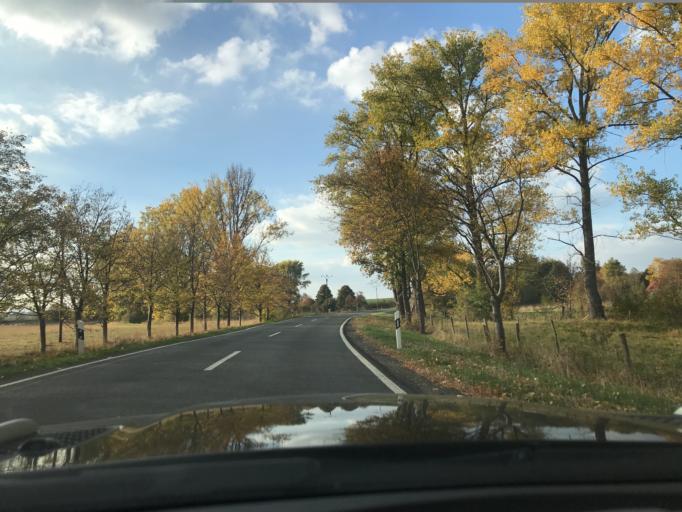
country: DE
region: Thuringia
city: Schonstedt
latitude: 51.1179
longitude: 10.5740
